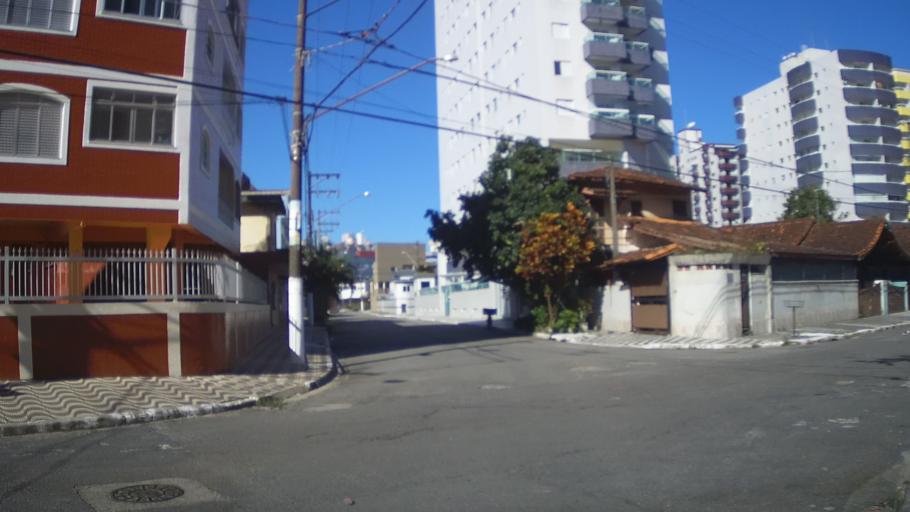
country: BR
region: Sao Paulo
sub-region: Praia Grande
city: Praia Grande
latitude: -24.0315
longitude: -46.4842
